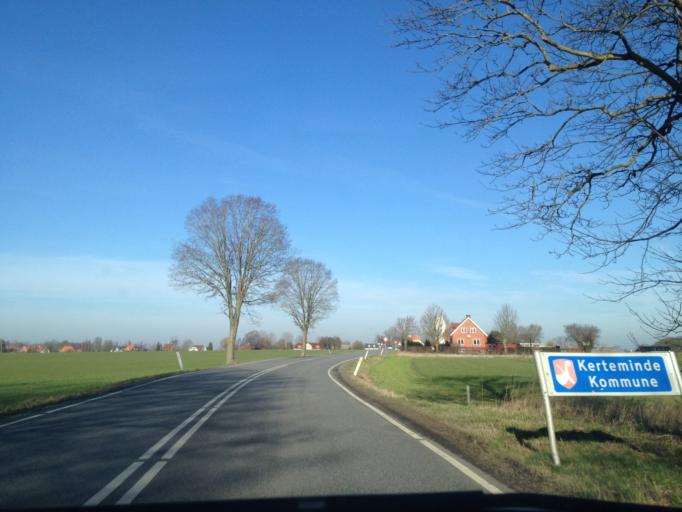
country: DK
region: South Denmark
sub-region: Kerteminde Kommune
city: Kerteminde
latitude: 55.4128
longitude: 10.6601
